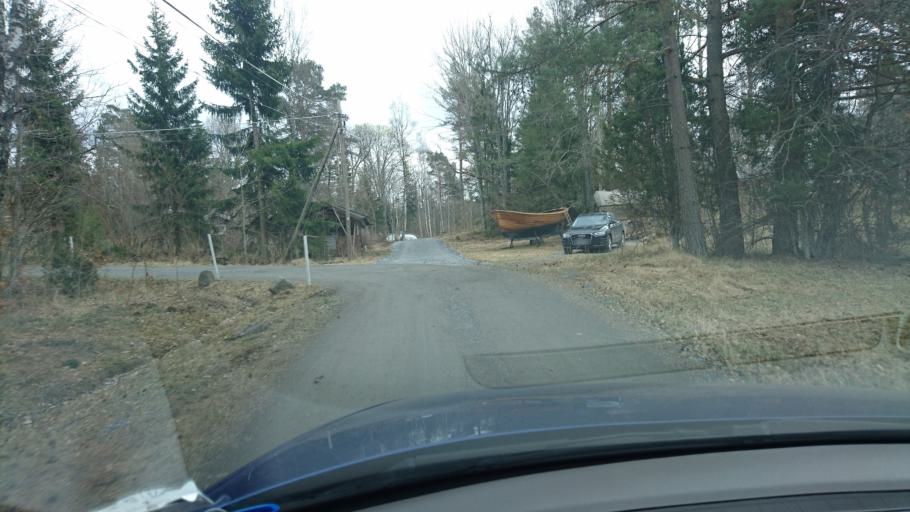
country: SE
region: Stockholm
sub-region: Norrtalje Kommun
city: Bjorko
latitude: 59.7917
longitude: 18.9962
